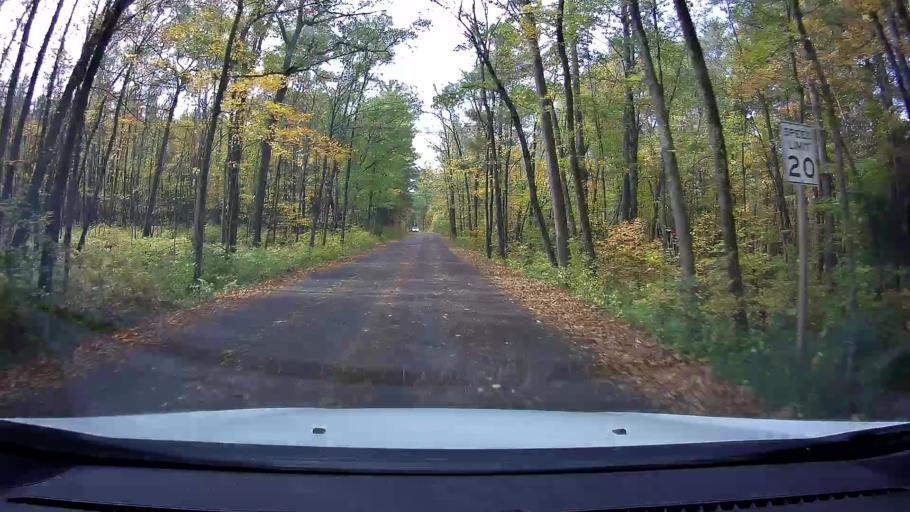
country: US
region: Wisconsin
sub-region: Polk County
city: Saint Croix Falls
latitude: 45.3904
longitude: -92.6531
